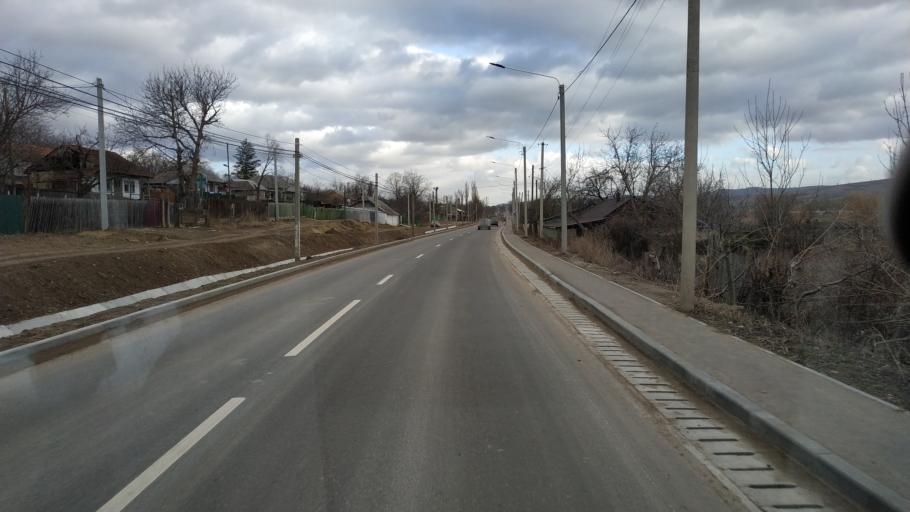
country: MD
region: Calarasi
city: Calarasi
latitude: 47.2833
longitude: 28.2039
